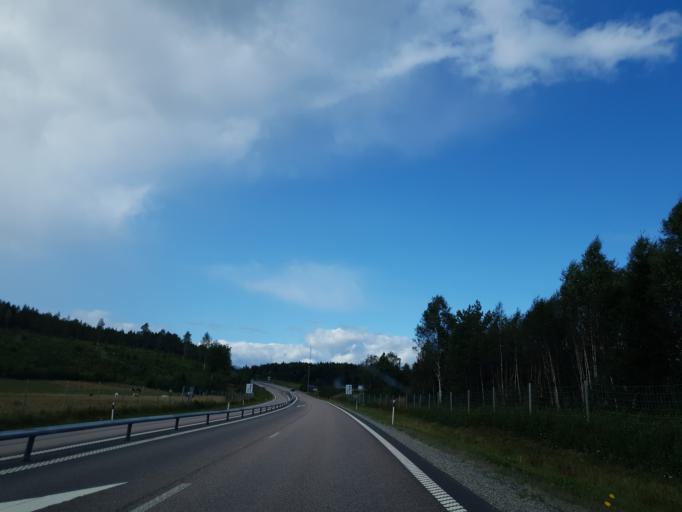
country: SE
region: Vaesternorrland
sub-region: OErnskoeldsviks Kommun
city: Ornskoldsvik
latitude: 63.3083
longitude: 18.8443
